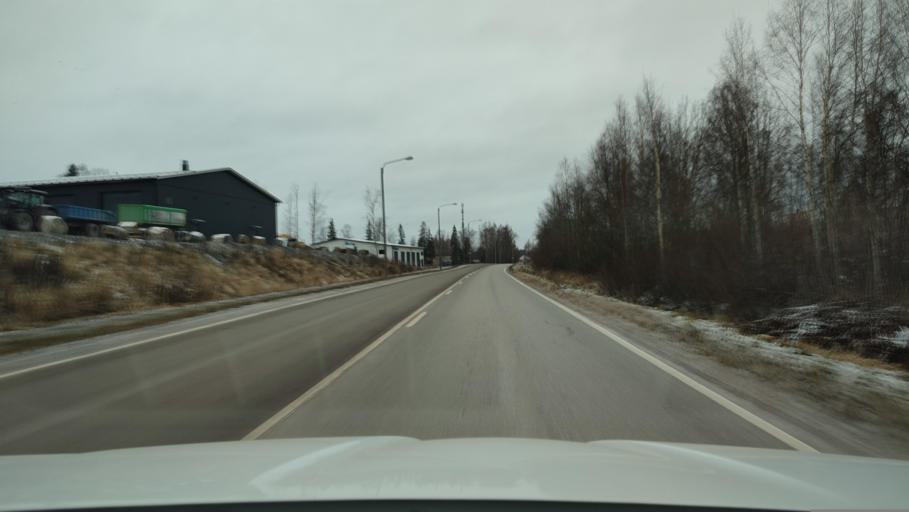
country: FI
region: Ostrobothnia
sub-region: Vaasa
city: Smedsby
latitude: 63.1163
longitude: 21.7155
